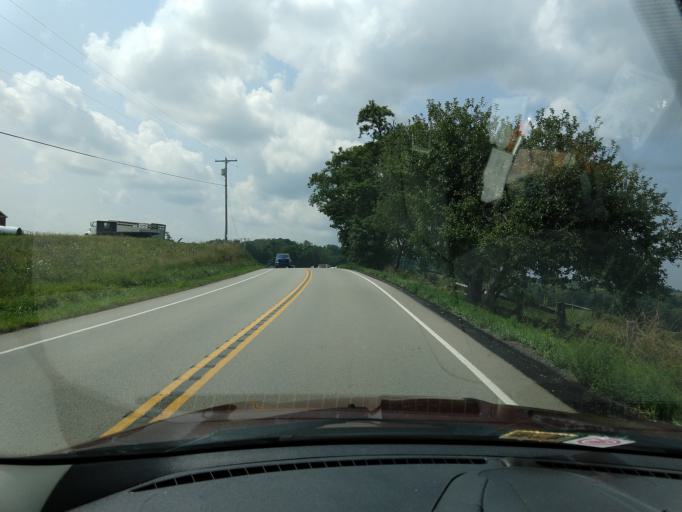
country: US
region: Pennsylvania
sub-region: Washington County
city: McMurray
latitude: 40.1873
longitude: -80.0772
